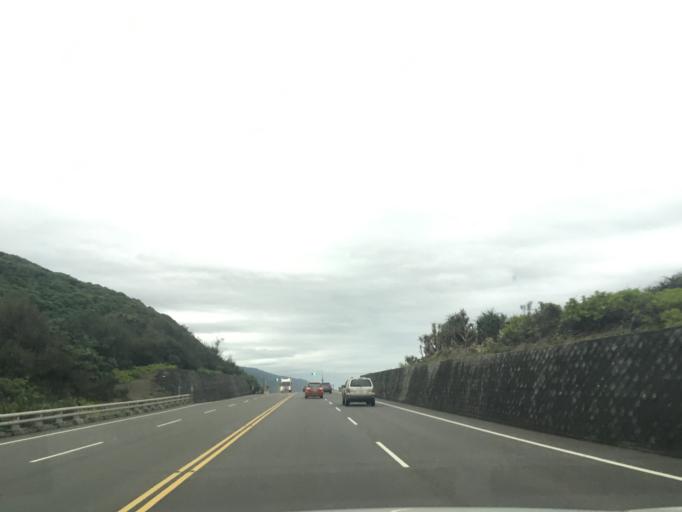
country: TW
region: Taiwan
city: Hengchun
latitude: 22.3090
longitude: 120.8904
